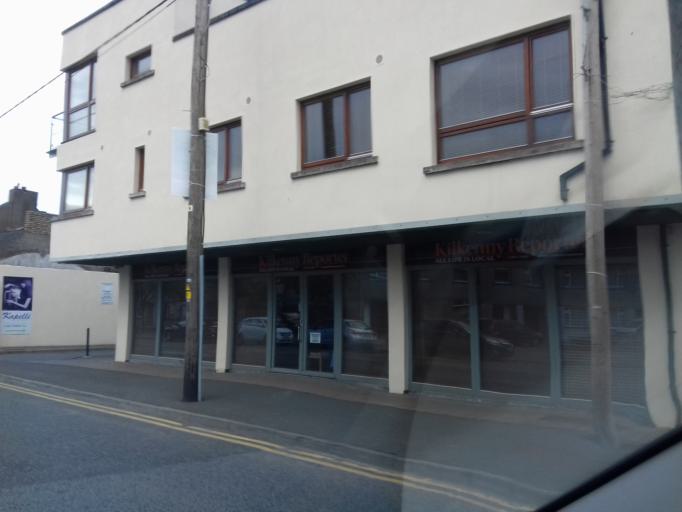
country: IE
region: Leinster
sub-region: Kilkenny
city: Kilkenny
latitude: 52.6465
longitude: -7.2509
